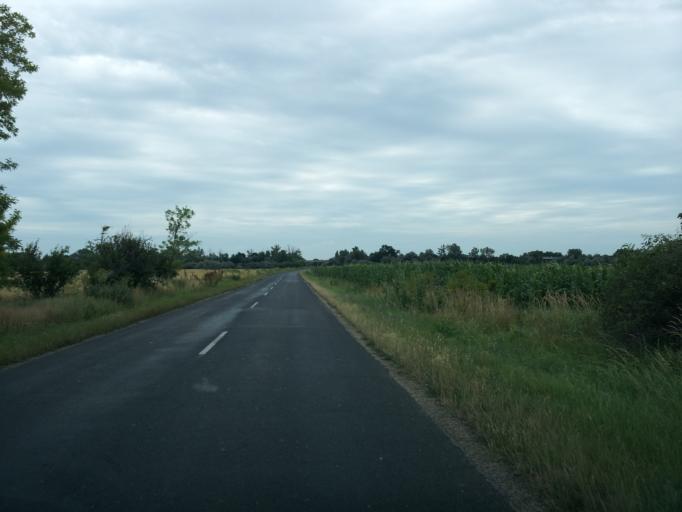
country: HU
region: Fejer
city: Lepseny
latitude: 47.0111
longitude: 18.2253
